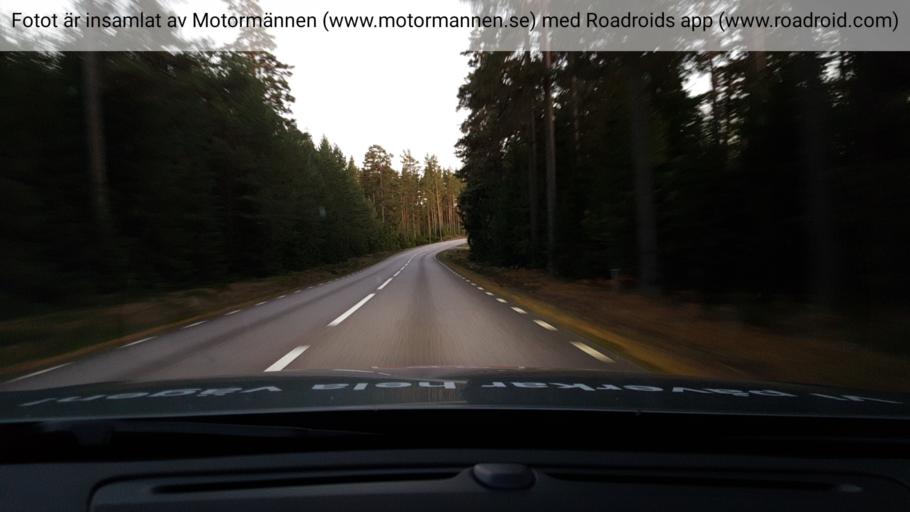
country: SE
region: OErebro
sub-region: Laxa Kommun
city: Laxa
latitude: 58.9284
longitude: 14.6553
